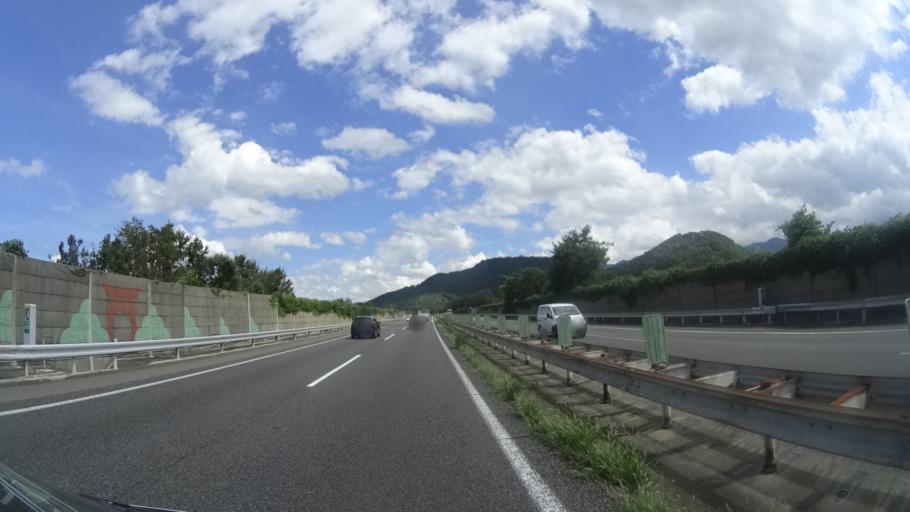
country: JP
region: Shiga Prefecture
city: Hikone
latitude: 35.1981
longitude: 136.2828
